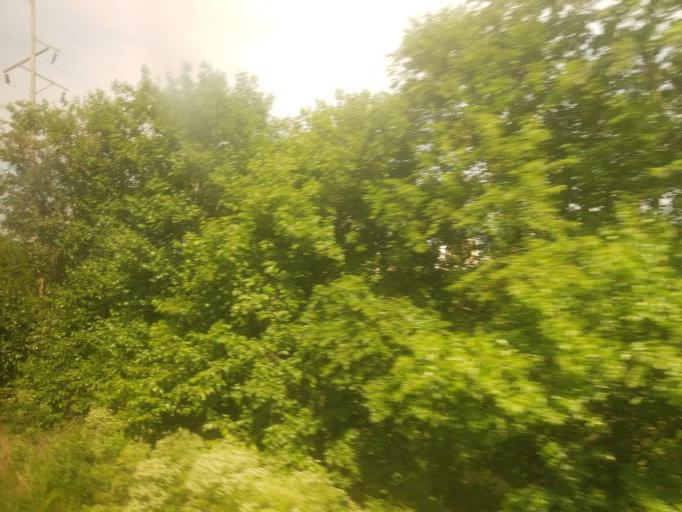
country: US
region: Illinois
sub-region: Knox County
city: Knoxville
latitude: 41.0340
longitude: -90.2729
